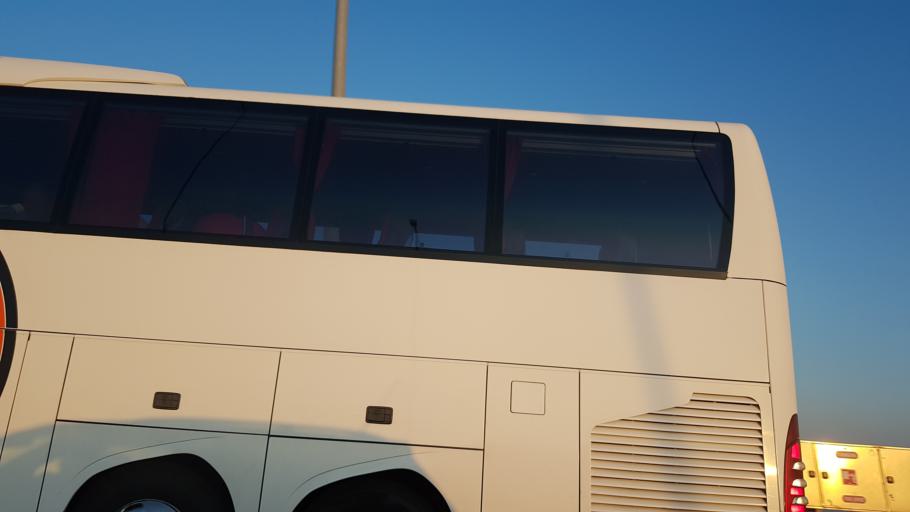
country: TR
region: Kocaeli
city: Tavsancil
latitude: 40.7592
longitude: 29.5165
